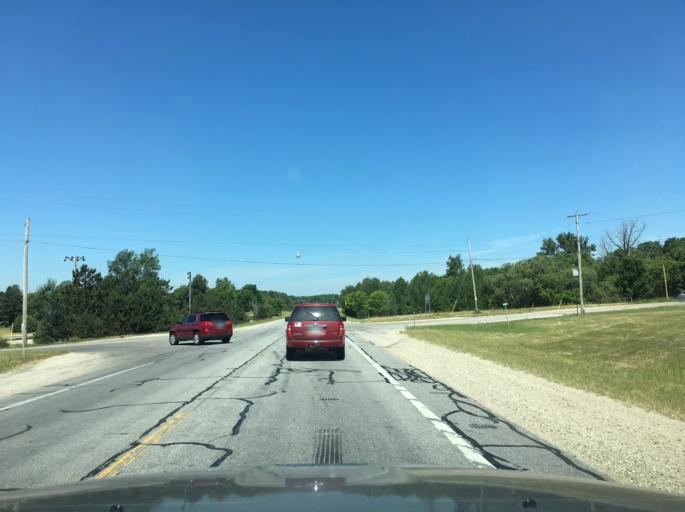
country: US
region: Michigan
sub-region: Osceola County
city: Reed City
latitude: 43.8796
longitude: -85.5026
